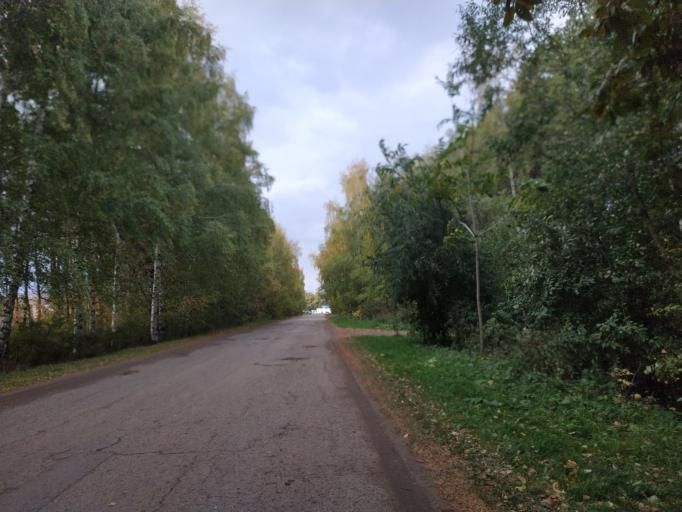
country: RU
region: Chuvashia
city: Ishley
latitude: 56.1298
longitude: 47.0891
